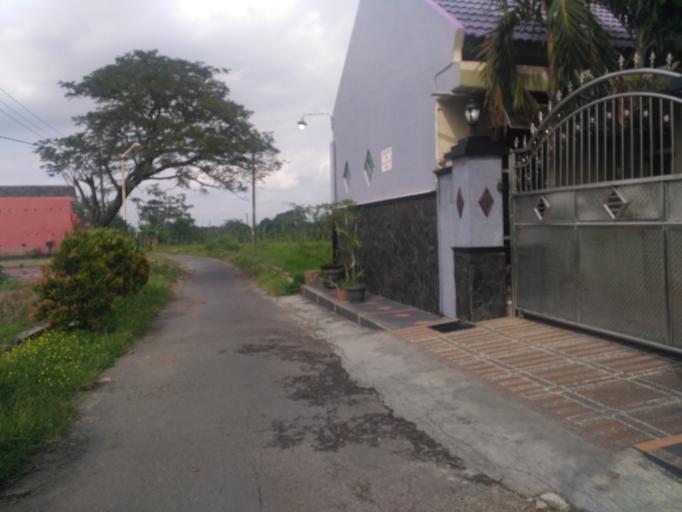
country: ID
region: Daerah Istimewa Yogyakarta
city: Yogyakarta
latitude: -7.7625
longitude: 110.3529
